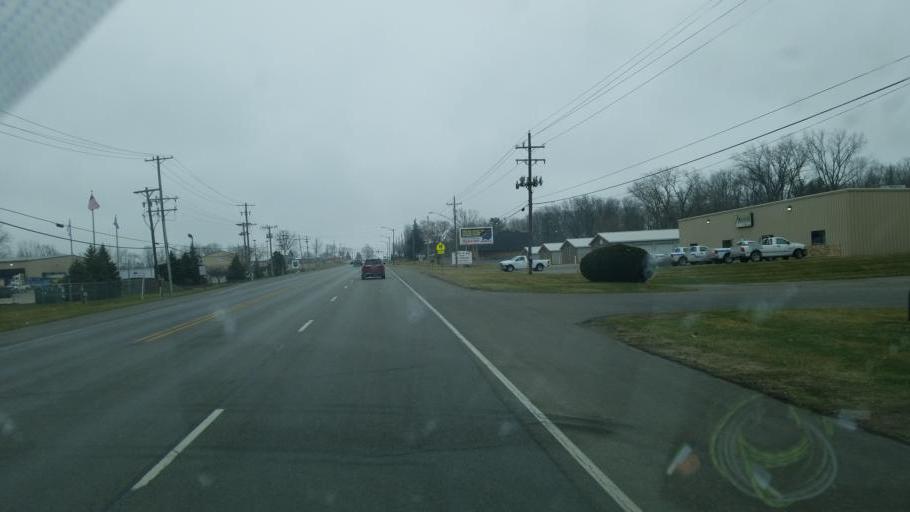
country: US
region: Indiana
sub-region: Wabash County
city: Wabash
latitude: 40.7861
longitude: -85.8202
